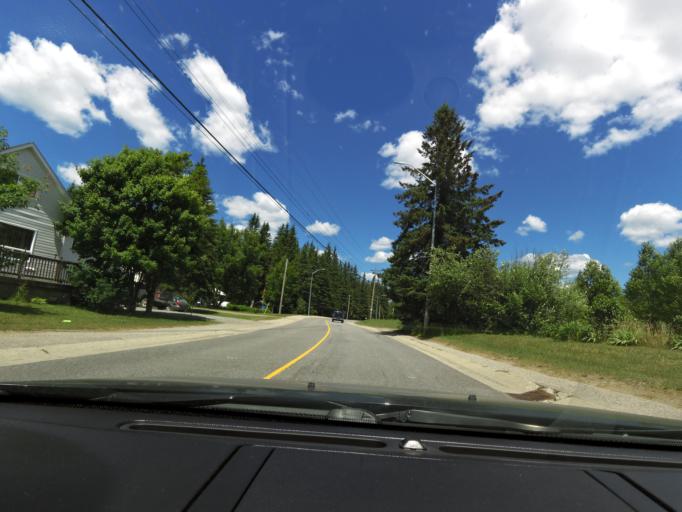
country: CA
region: Ontario
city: Huntsville
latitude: 45.5608
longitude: -79.2280
